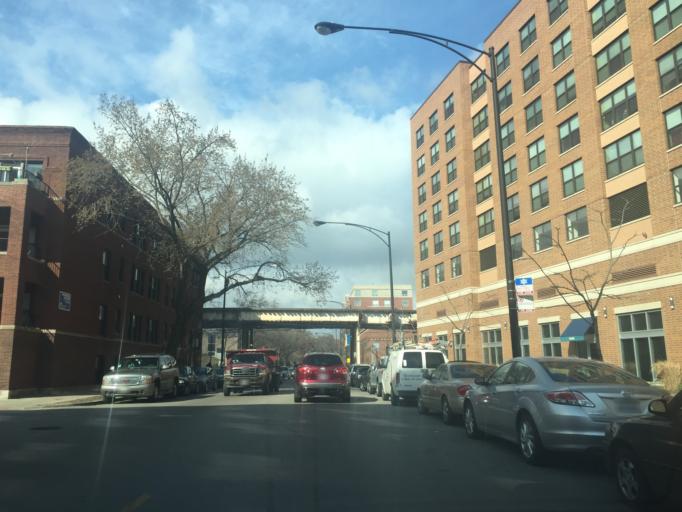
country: US
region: Illinois
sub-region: Cook County
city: Lincolnwood
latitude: 41.9618
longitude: -87.6562
